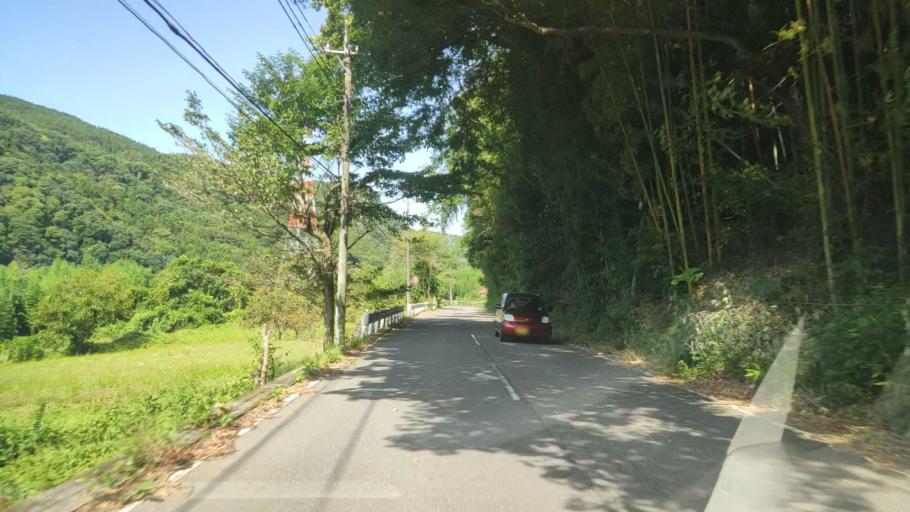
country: JP
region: Gunma
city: Numata
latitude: 36.5919
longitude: 139.0537
